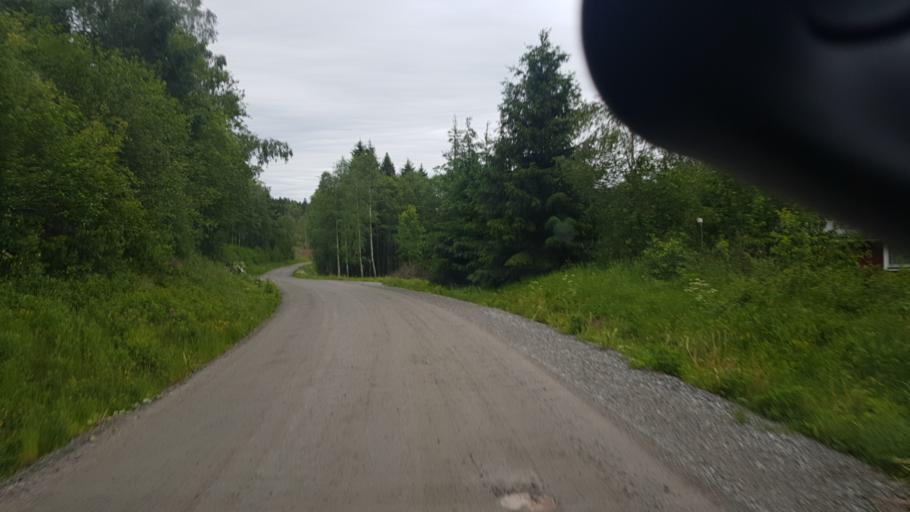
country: NO
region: Ostfold
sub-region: Romskog
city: Romskog
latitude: 59.6826
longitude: 11.9313
